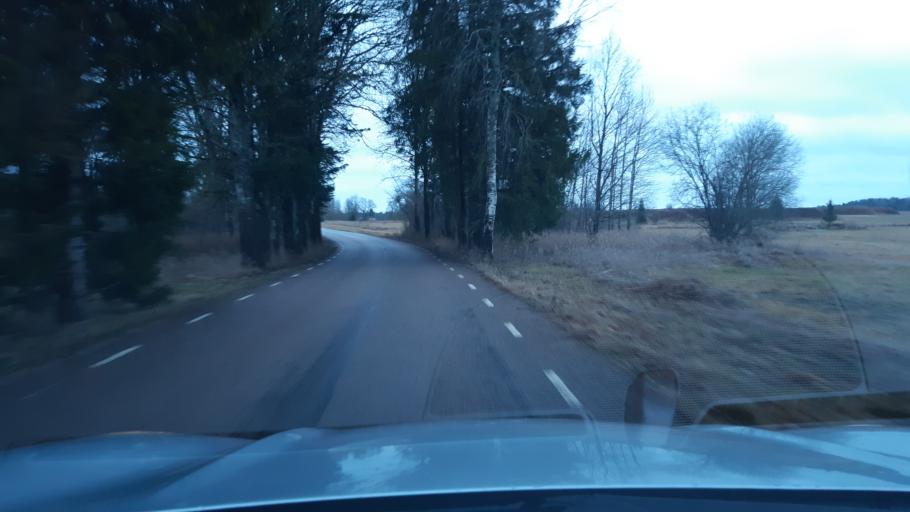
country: EE
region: Raplamaa
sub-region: Rapla vald
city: Rapla
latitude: 58.9967
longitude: 24.7189
